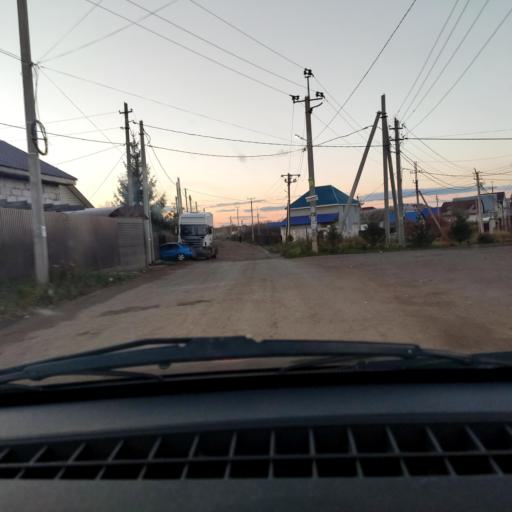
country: RU
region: Bashkortostan
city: Ufa
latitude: 54.6407
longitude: 55.9183
